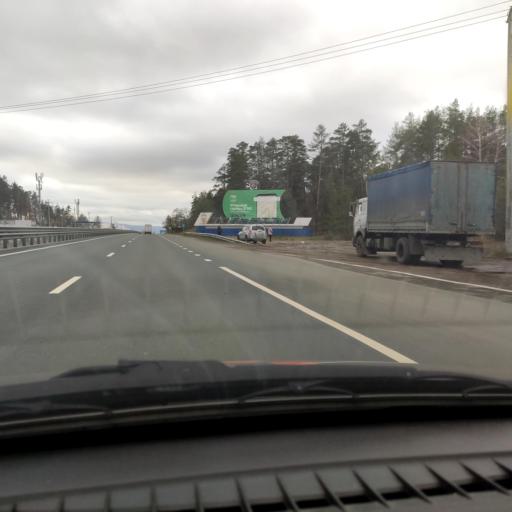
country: RU
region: Samara
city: Zhigulevsk
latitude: 53.5060
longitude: 49.5543
